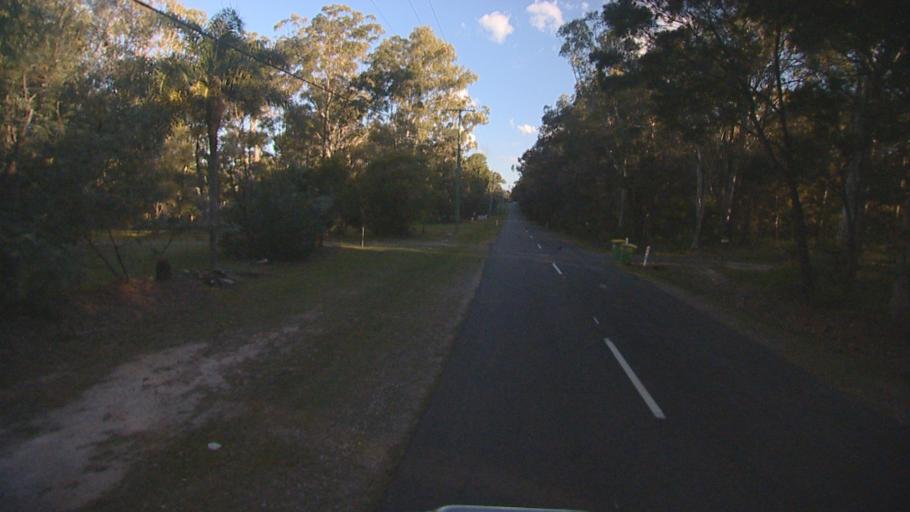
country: AU
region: Queensland
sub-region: Gold Coast
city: Yatala
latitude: -27.6800
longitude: 153.2753
